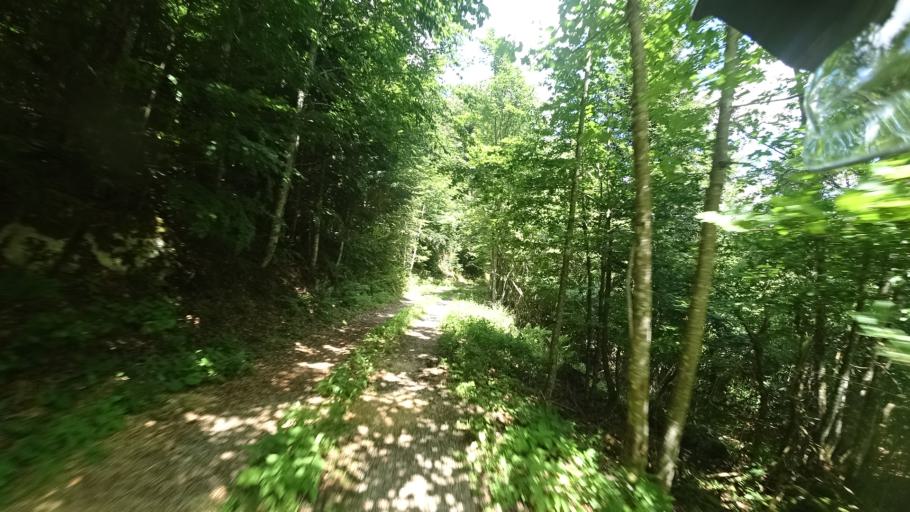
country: SI
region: Osilnica
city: Osilnica
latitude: 45.4895
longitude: 14.7187
